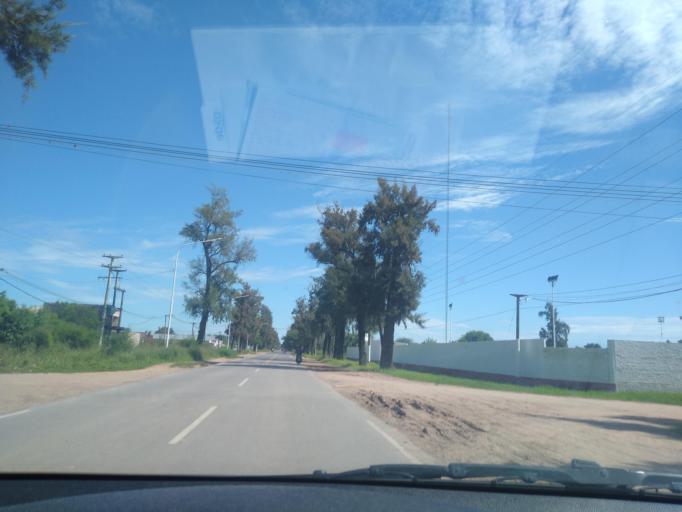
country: AR
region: Chaco
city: Presidencia Roque Saenz Pena
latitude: -26.7731
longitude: -60.4176
